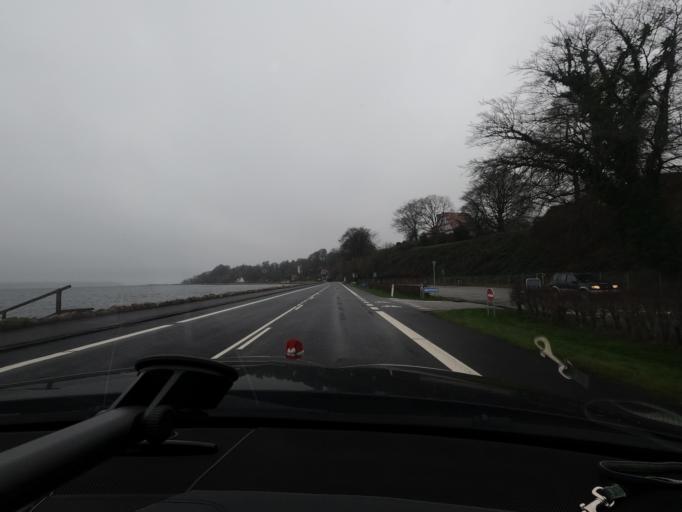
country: DE
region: Schleswig-Holstein
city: Wees
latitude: 54.8594
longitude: 9.4960
